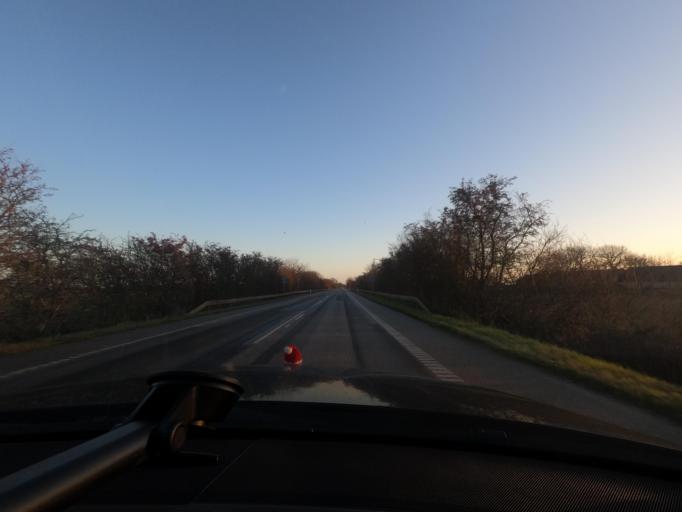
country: DK
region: South Denmark
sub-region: Sonderborg Kommune
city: Horuphav
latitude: 54.8936
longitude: 9.9689
